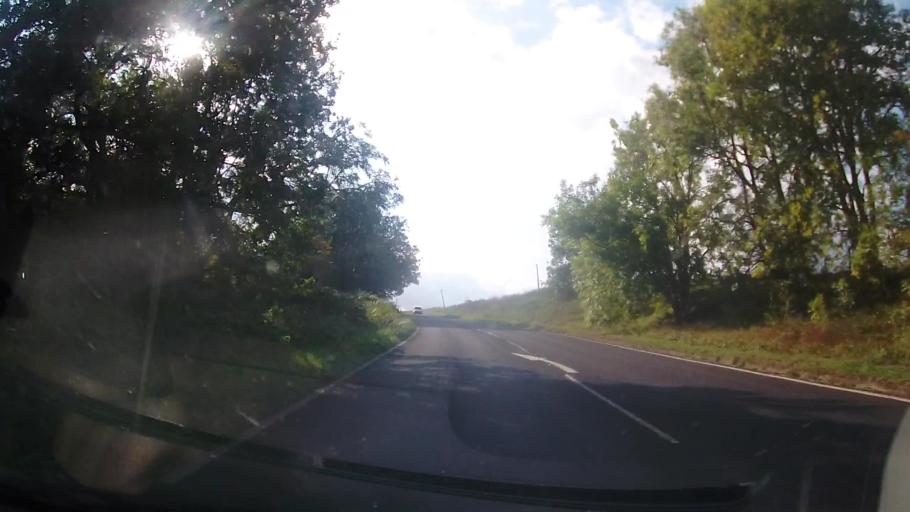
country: GB
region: England
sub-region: Kent
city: Hythe
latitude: 51.0941
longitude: 1.0902
